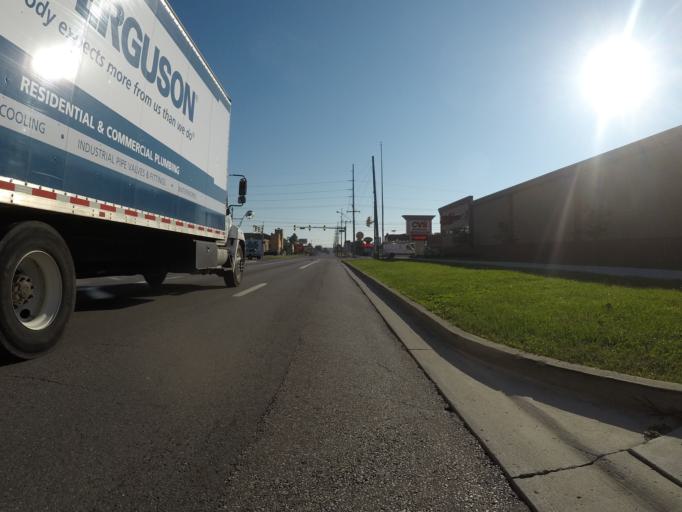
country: US
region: West Virginia
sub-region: Cabell County
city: Huntington
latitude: 38.4229
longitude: -82.4234
